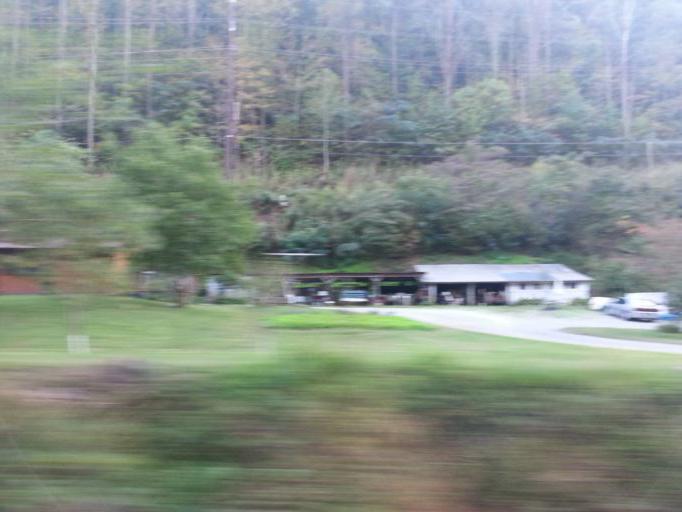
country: US
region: Tennessee
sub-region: Sevier County
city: Pigeon Forge
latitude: 35.6903
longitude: -83.6977
